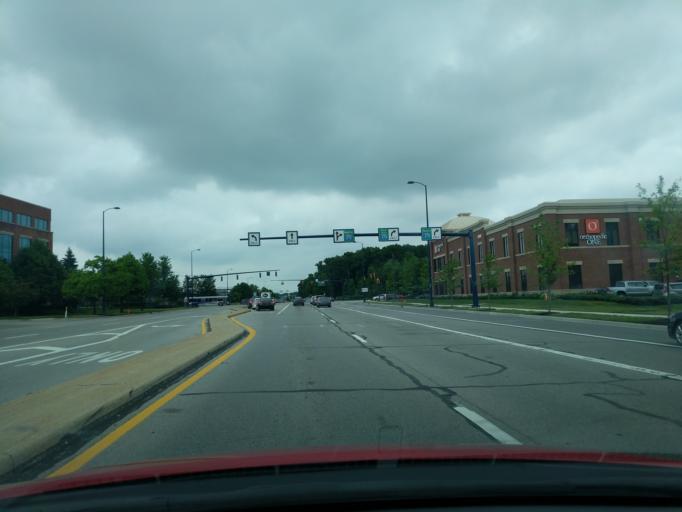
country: US
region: Ohio
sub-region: Franklin County
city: Gahanna
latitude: 40.0468
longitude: -82.9089
